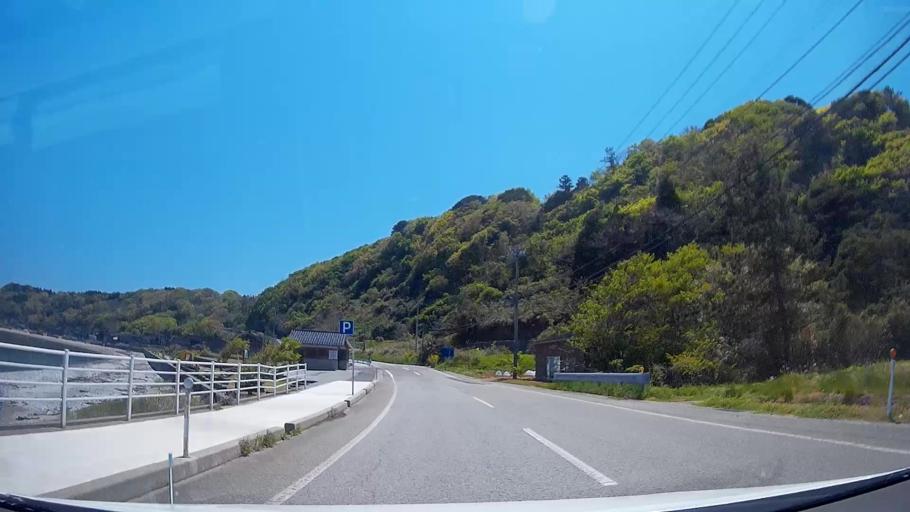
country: JP
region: Ishikawa
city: Nanao
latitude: 37.5262
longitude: 137.2949
